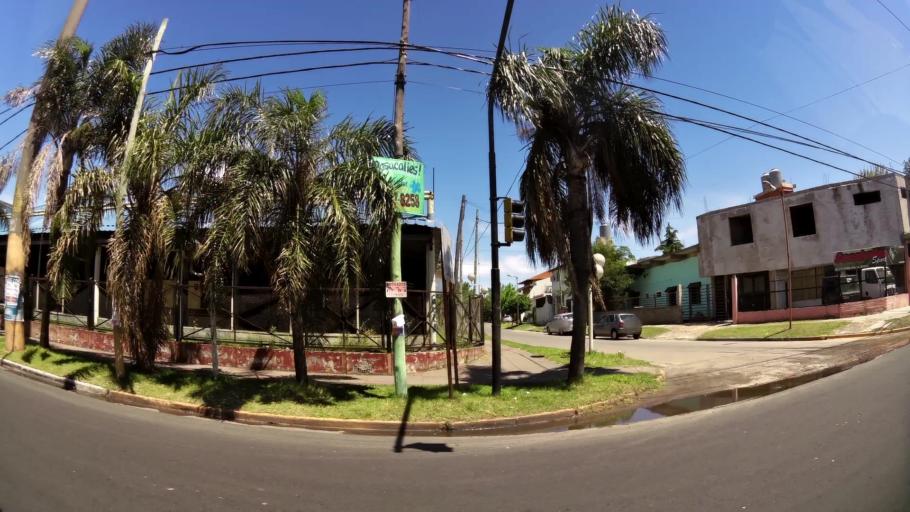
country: AR
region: Buenos Aires
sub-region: Partido de Quilmes
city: Quilmes
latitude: -34.7385
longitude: -58.2764
